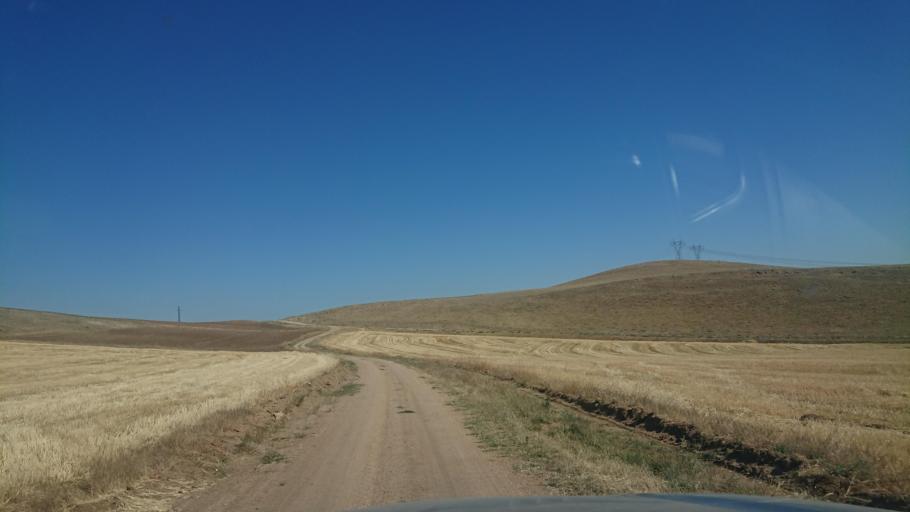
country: TR
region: Aksaray
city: Agacoren
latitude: 38.9123
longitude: 33.8966
